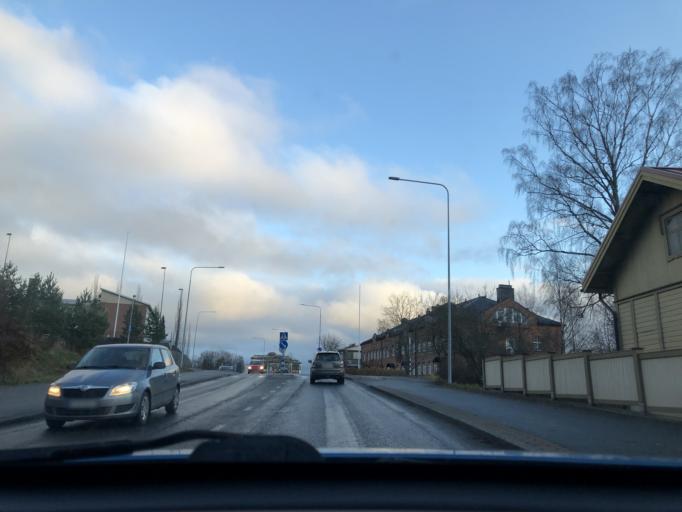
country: FI
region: Pirkanmaa
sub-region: Tampere
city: Kangasala
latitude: 61.4639
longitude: 24.0612
